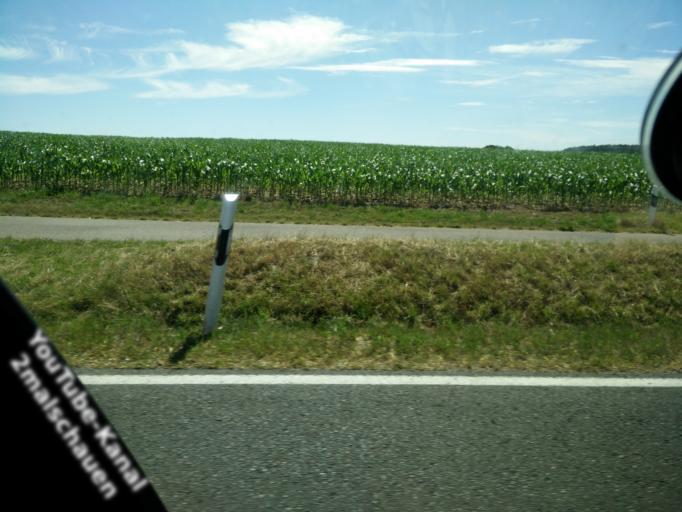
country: DE
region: Saxony
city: Waldheim
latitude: 51.0852
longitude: 13.0385
